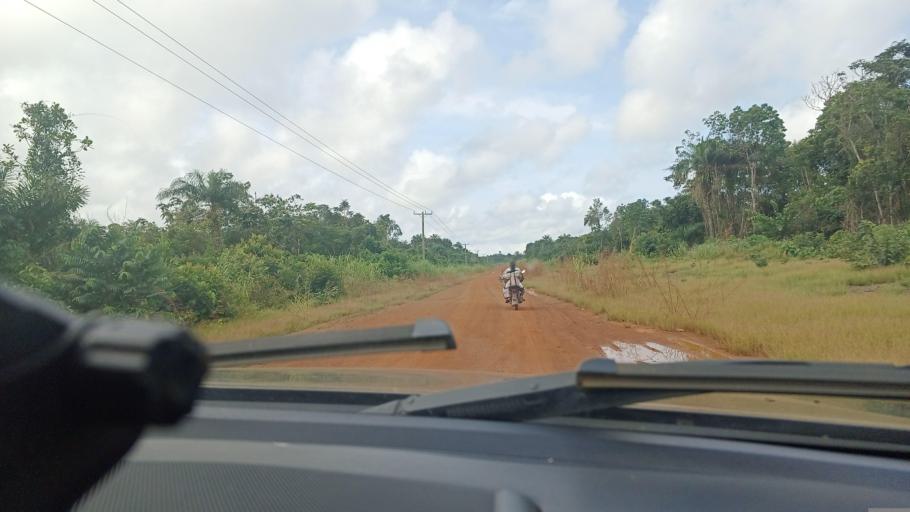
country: LR
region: Grand Cape Mount
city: Robertsport
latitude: 6.6826
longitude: -11.1300
